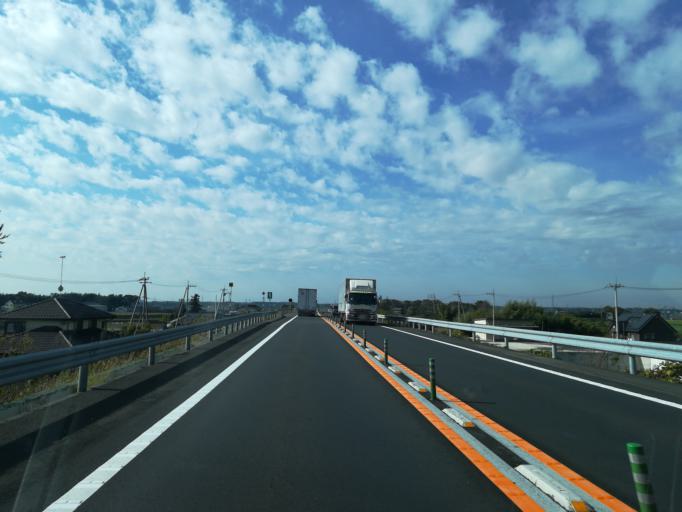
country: JP
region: Ibaraki
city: Ishige
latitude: 36.0730
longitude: 139.9524
